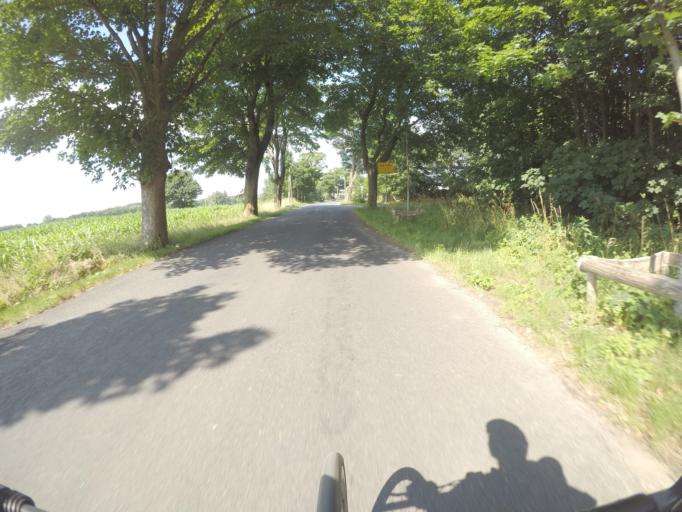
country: DE
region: Mecklenburg-Vorpommern
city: Gingst
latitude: 54.4368
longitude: 13.2219
